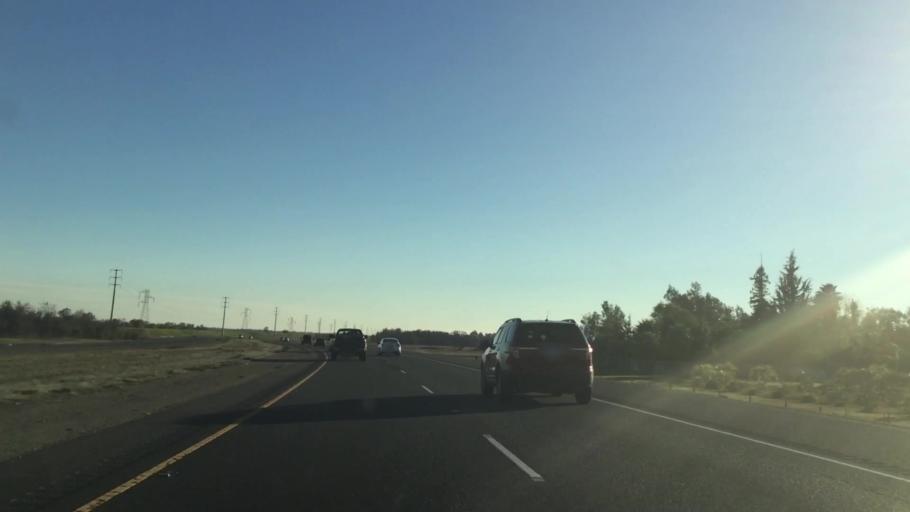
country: US
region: California
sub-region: Yuba County
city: Olivehurst
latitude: 39.0578
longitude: -121.5441
